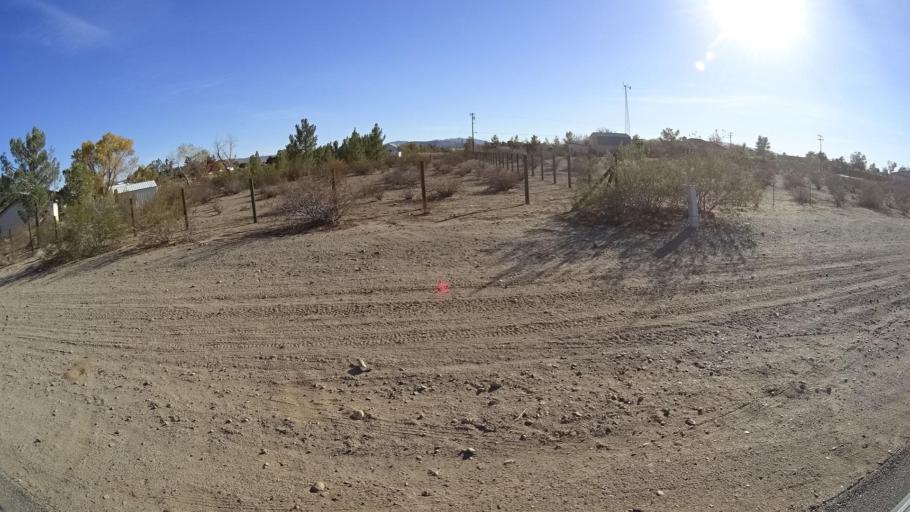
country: US
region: California
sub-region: Kern County
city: Ridgecrest
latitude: 35.6375
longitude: -117.7044
